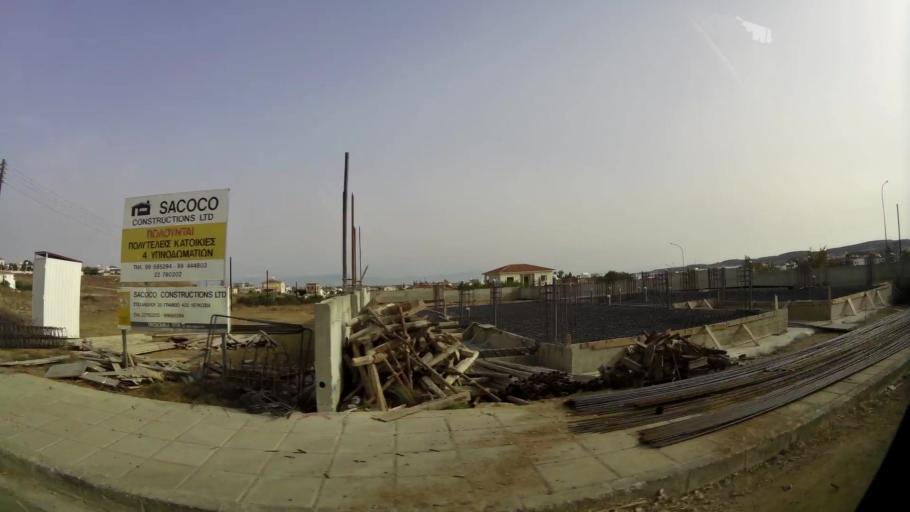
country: CY
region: Lefkosia
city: Geri
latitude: 35.0676
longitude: 33.3931
